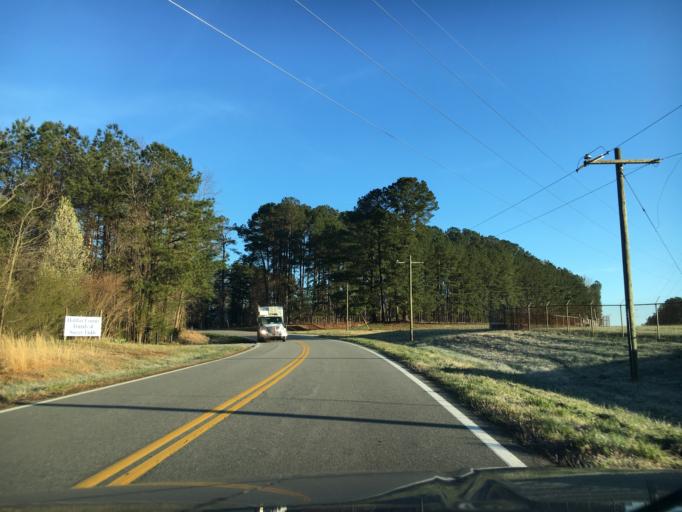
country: US
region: Virginia
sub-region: Halifax County
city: Halifax
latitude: 36.7665
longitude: -78.9165
